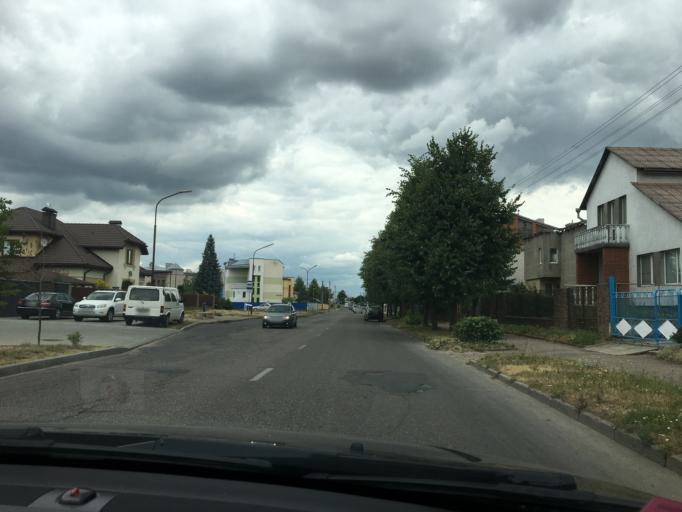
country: BY
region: Grodnenskaya
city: Hrodna
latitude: 53.6272
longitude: 23.8502
